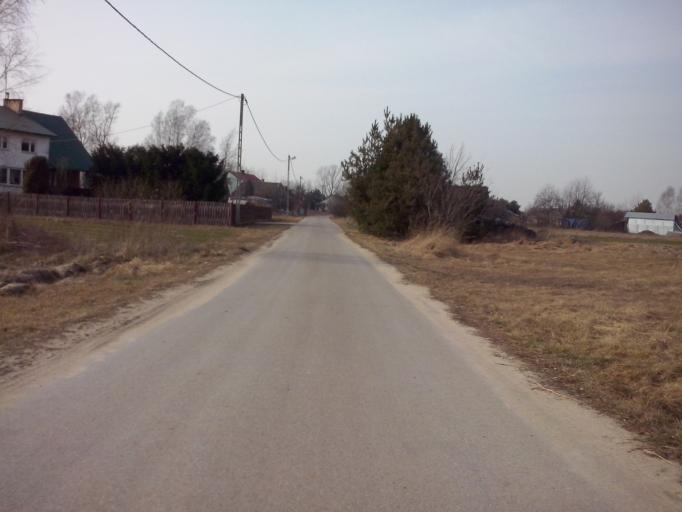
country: PL
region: Subcarpathian Voivodeship
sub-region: Powiat nizanski
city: Krzeszow
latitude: 50.4230
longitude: 22.3656
